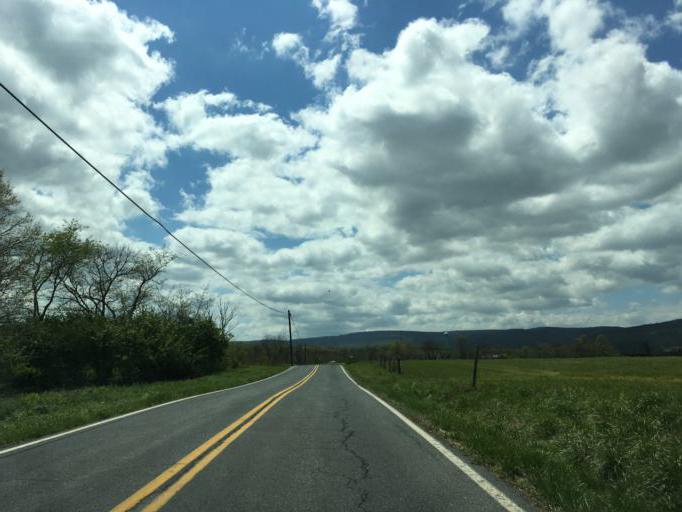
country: US
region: Maryland
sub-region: Frederick County
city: Thurmont
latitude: 39.6302
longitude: -77.3760
